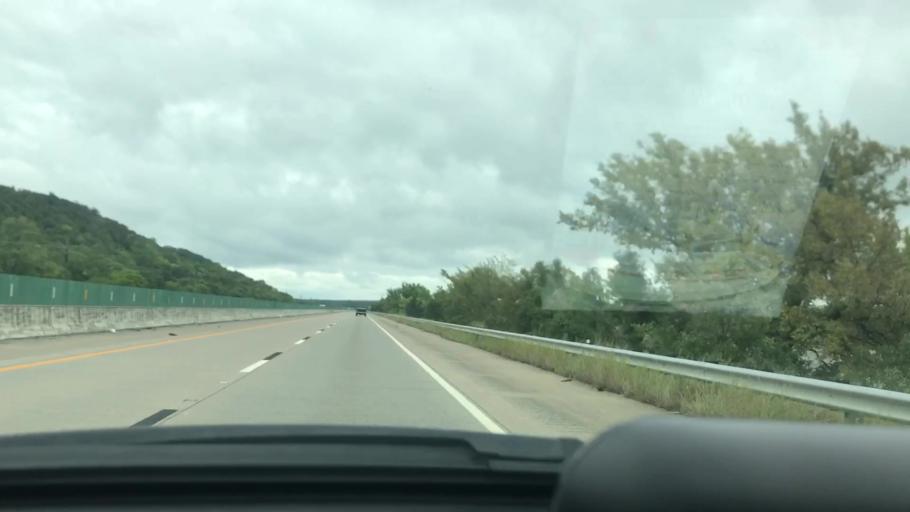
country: US
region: Oklahoma
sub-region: Pittsburg County
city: Krebs
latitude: 35.1170
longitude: -95.6860
